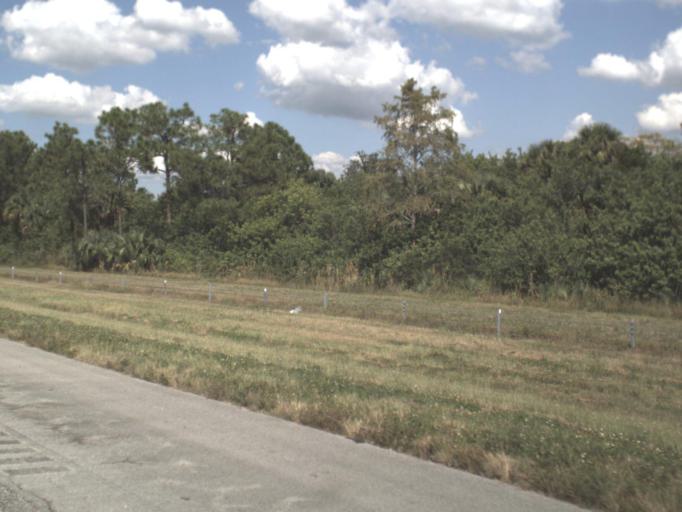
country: US
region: Florida
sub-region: Indian River County
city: West Vero Corridor
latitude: 27.5087
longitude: -80.5872
